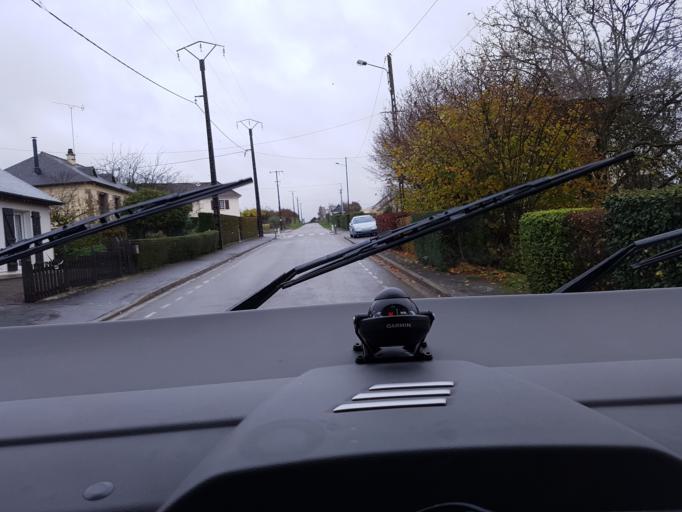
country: FR
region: Pays de la Loire
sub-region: Departement de la Mayenne
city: Montenay
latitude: 48.2895
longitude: -0.8912
